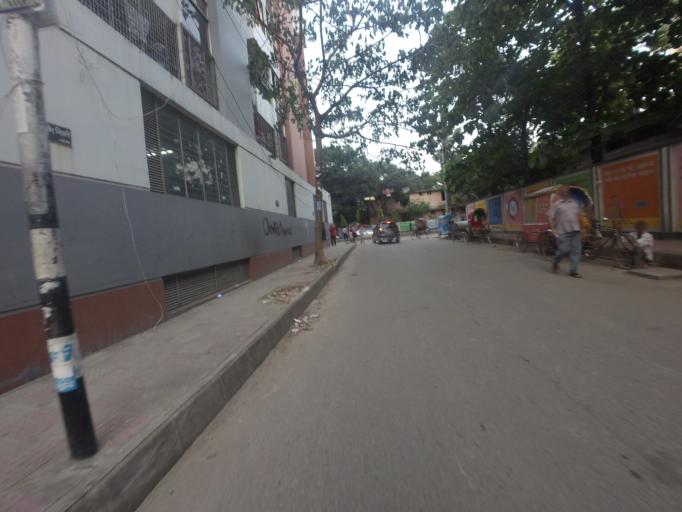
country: BD
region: Dhaka
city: Azimpur
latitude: 23.7633
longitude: 90.3654
